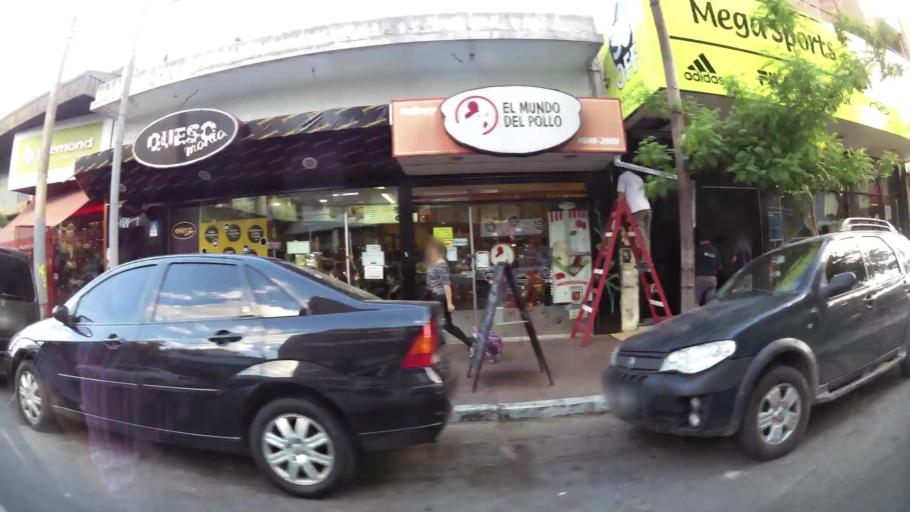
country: AR
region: Buenos Aires
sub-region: Partido de General San Martin
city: General San Martin
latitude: -34.5478
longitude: -58.5519
